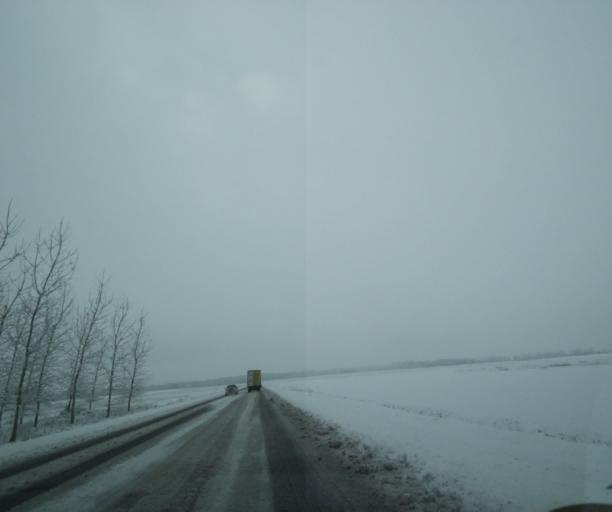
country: FR
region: Champagne-Ardenne
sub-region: Departement de la Haute-Marne
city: Saint-Dizier
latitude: 48.5983
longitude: 4.8953
